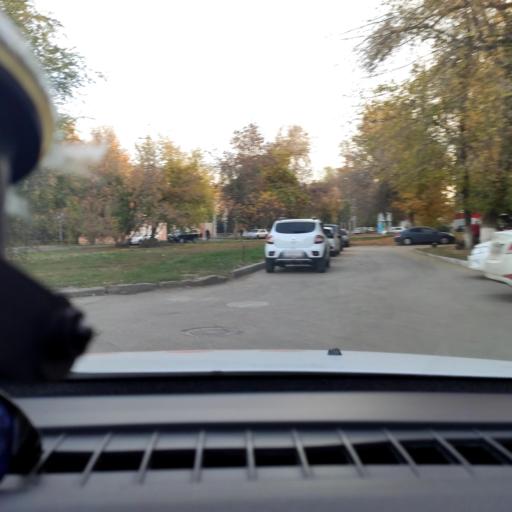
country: RU
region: Samara
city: Samara
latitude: 53.2022
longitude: 50.1330
